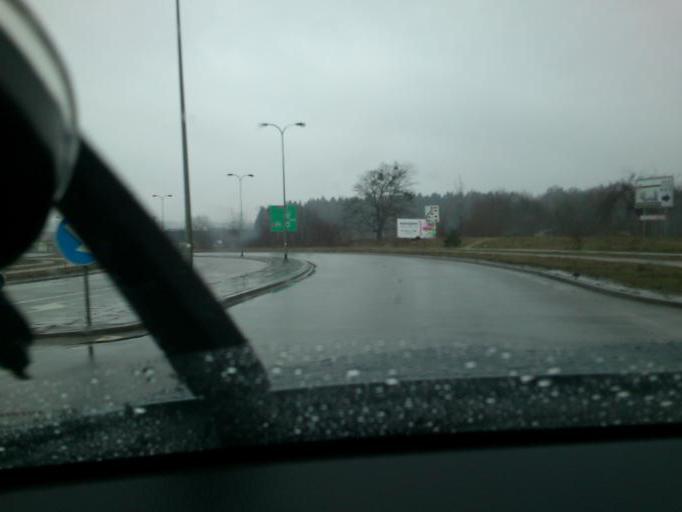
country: PL
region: Pomeranian Voivodeship
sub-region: Gdynia
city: Wielki Kack
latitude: 54.4125
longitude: 18.4810
